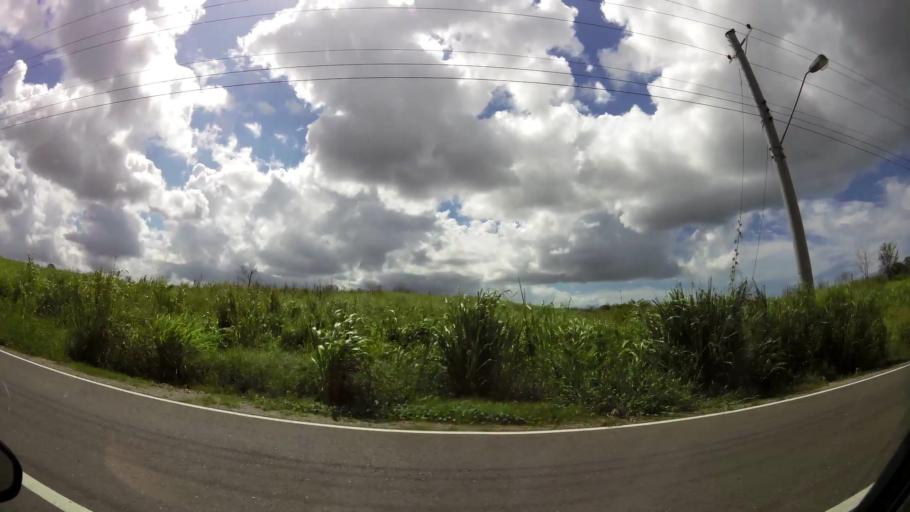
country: TT
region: Penal/Debe
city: Debe
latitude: 10.2349
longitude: -61.4957
